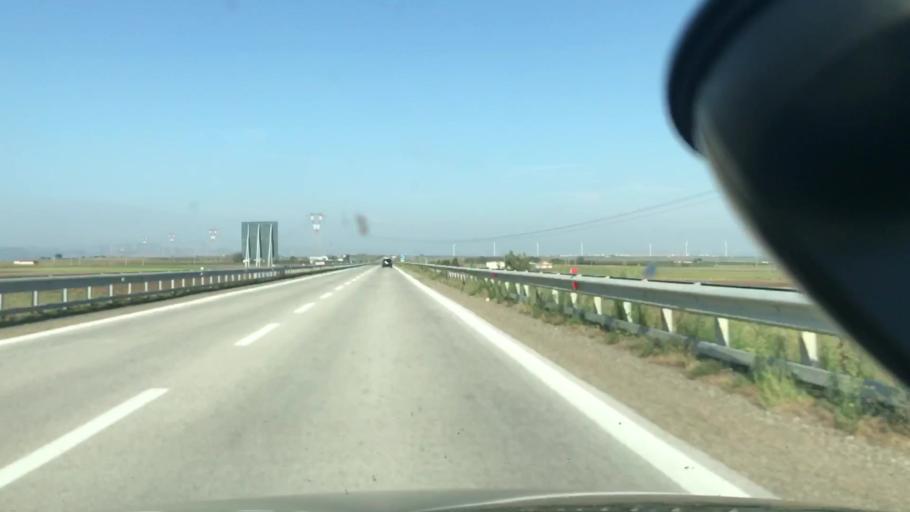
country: IT
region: Basilicate
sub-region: Provincia di Potenza
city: Venosa
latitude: 40.9963
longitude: 15.8800
